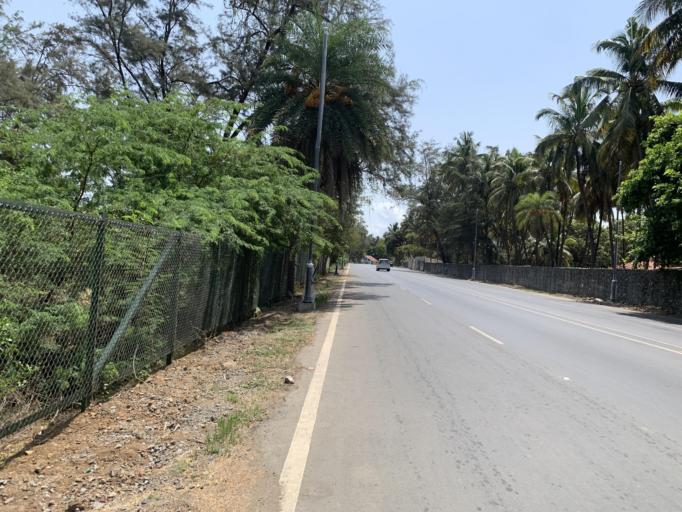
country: IN
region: Daman and Diu
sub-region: Daman District
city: Daman
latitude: 20.4622
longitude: 72.8500
